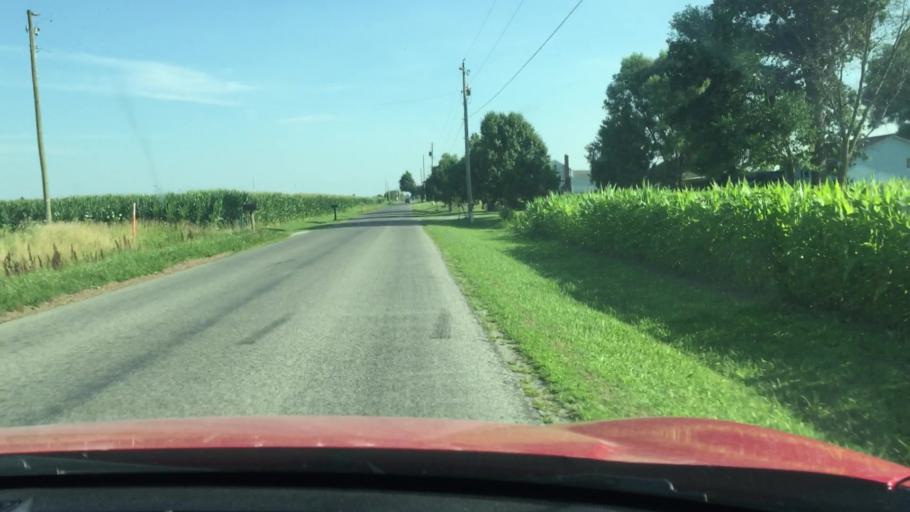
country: US
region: Ohio
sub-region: Hardin County
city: Ada
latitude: 40.7733
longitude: -83.8423
